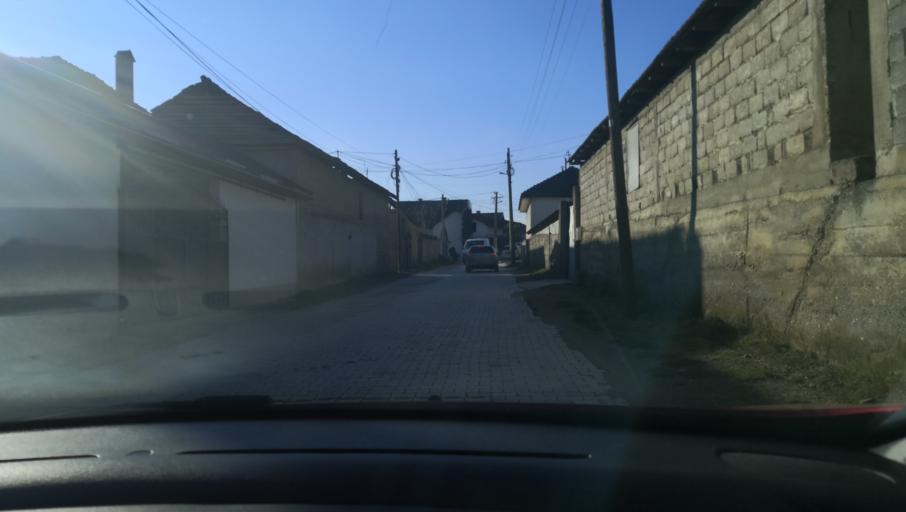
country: MK
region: Brvenica
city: Celopek
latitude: 41.9368
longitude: 21.0069
